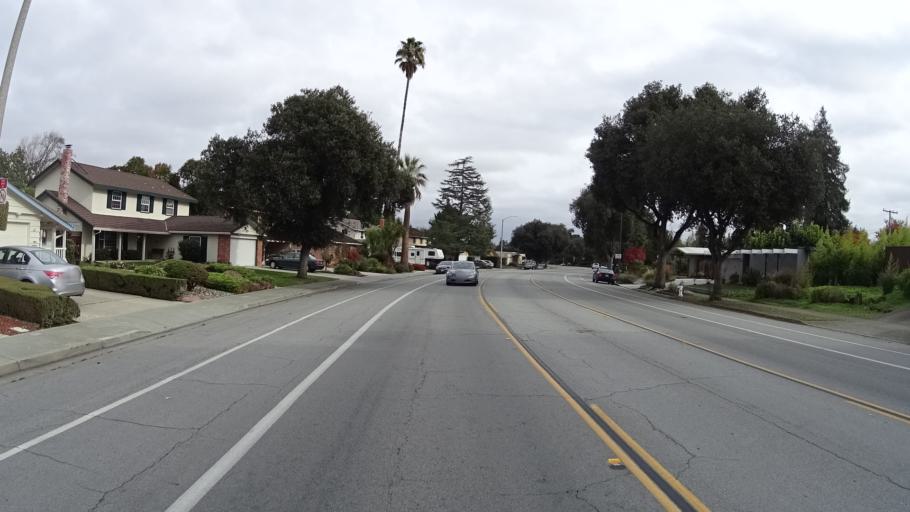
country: US
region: California
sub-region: Santa Clara County
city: Sunnyvale
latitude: 37.3595
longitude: -122.0400
